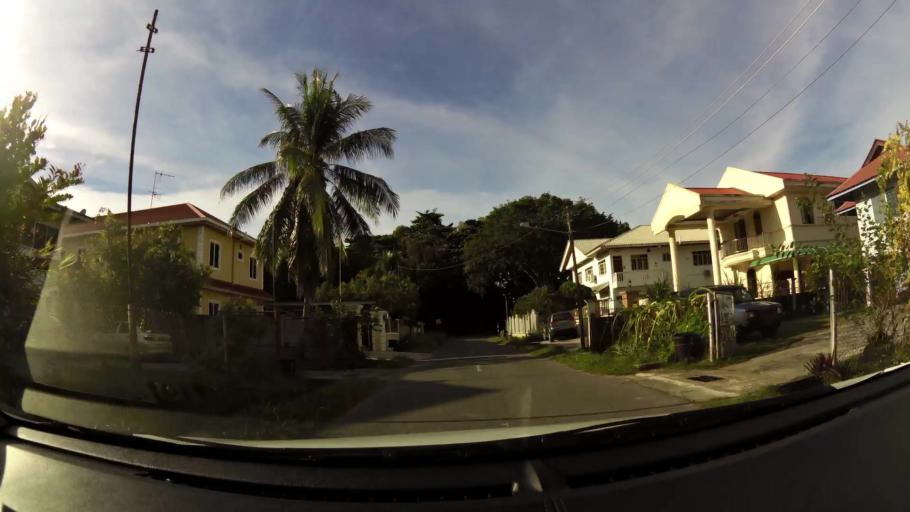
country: BN
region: Belait
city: Kuala Belait
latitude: 4.5860
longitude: 114.1949
